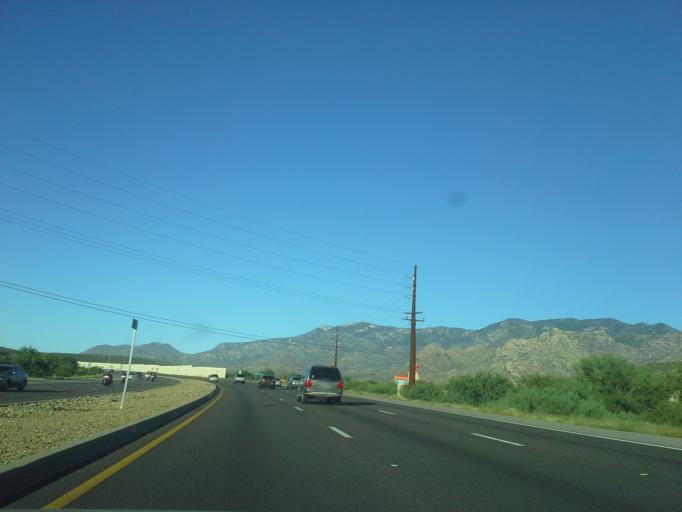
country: US
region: Arizona
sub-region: Pima County
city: Oro Valley
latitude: 32.4090
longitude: -110.9424
